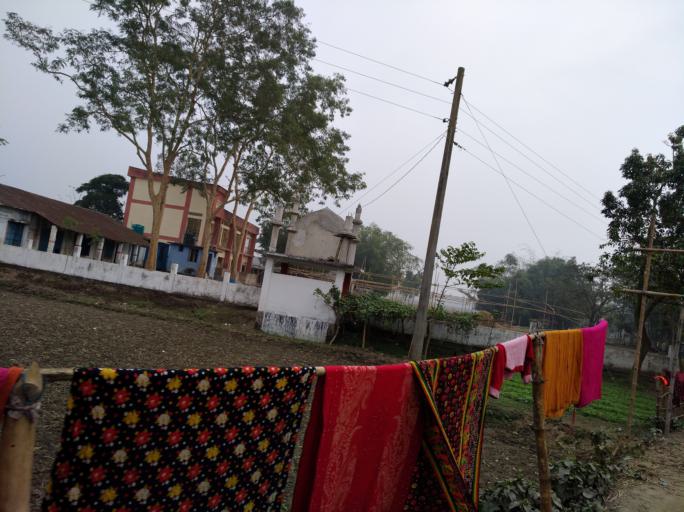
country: BD
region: Rajshahi
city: Saidpur
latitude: 25.9815
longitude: 88.9151
